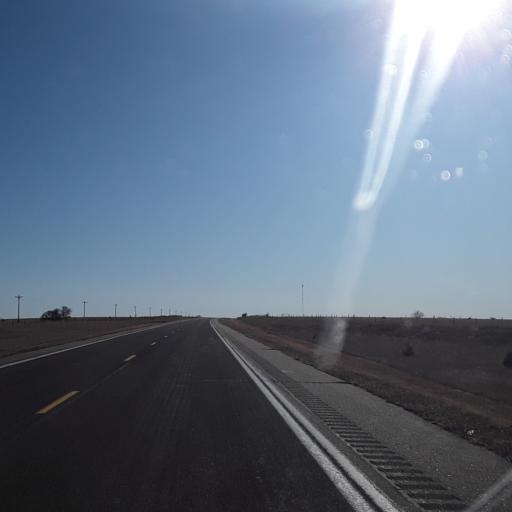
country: US
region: Nebraska
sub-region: Frontier County
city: Stockville
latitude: 40.6154
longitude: -100.6302
